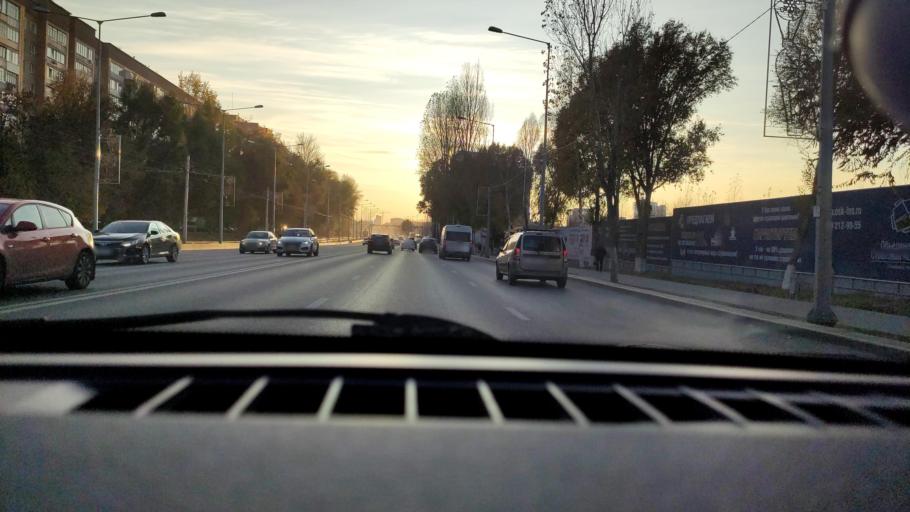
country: RU
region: Samara
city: Samara
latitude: 53.2188
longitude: 50.1534
